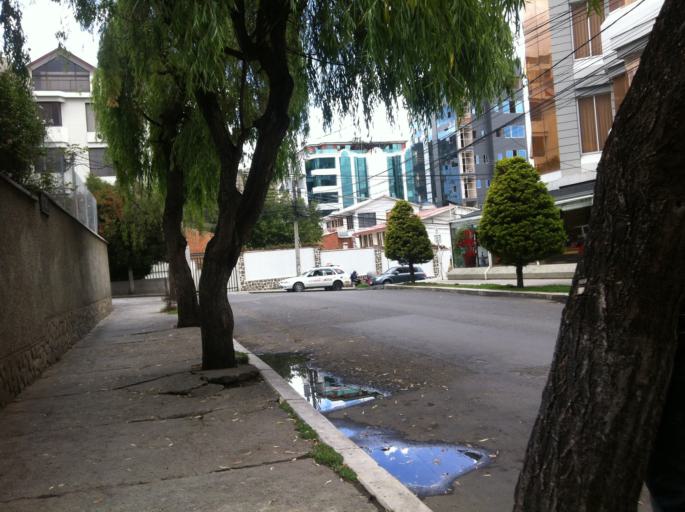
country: BO
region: La Paz
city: La Paz
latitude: -16.5395
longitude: -68.0787
